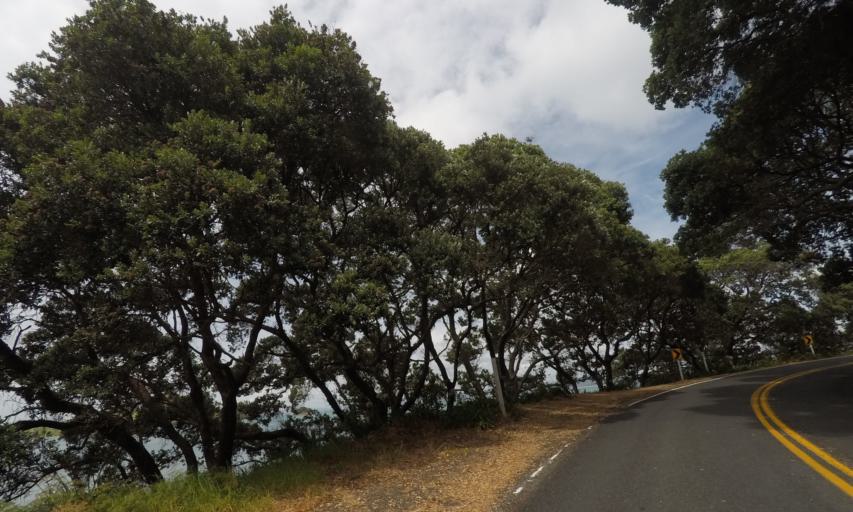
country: NZ
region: Northland
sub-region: Whangarei
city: Ruakaka
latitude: -35.8336
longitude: 174.5316
